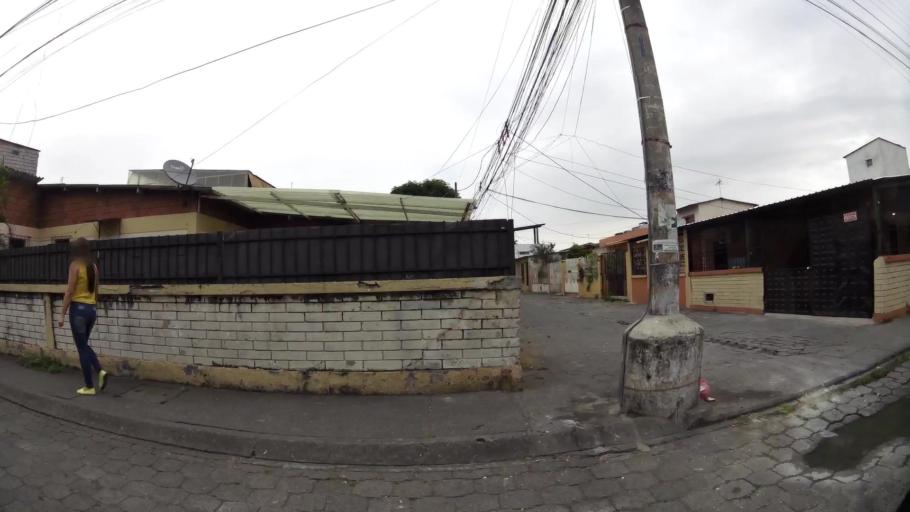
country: EC
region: Guayas
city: Eloy Alfaro
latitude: -2.1356
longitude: -79.8977
